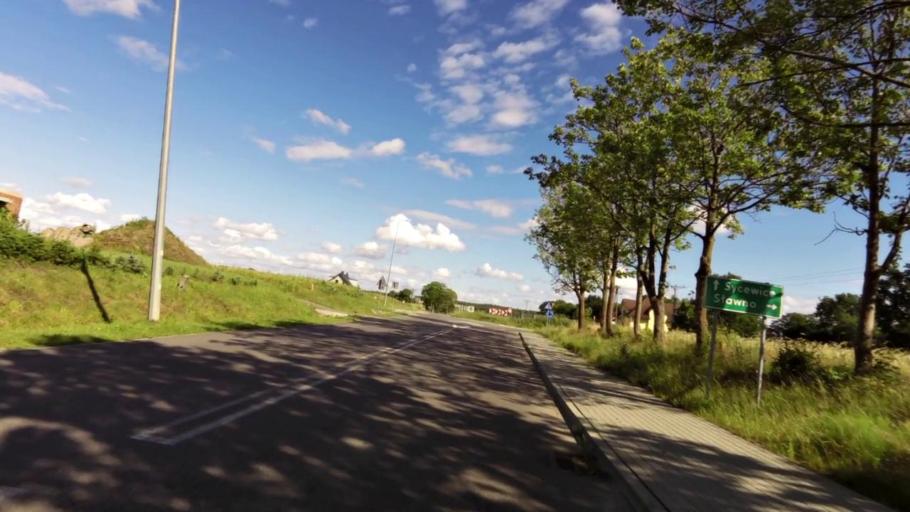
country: PL
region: West Pomeranian Voivodeship
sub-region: Powiat slawienski
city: Slawno
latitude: 54.4551
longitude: 16.7404
